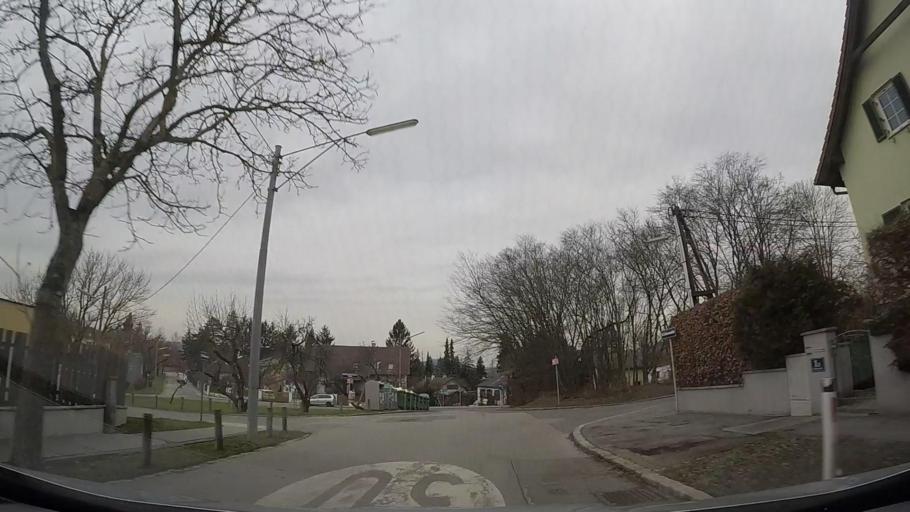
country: AT
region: Lower Austria
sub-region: Politischer Bezirk Wien-Umgebung
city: Purkersdorf
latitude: 48.2140
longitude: 16.2401
